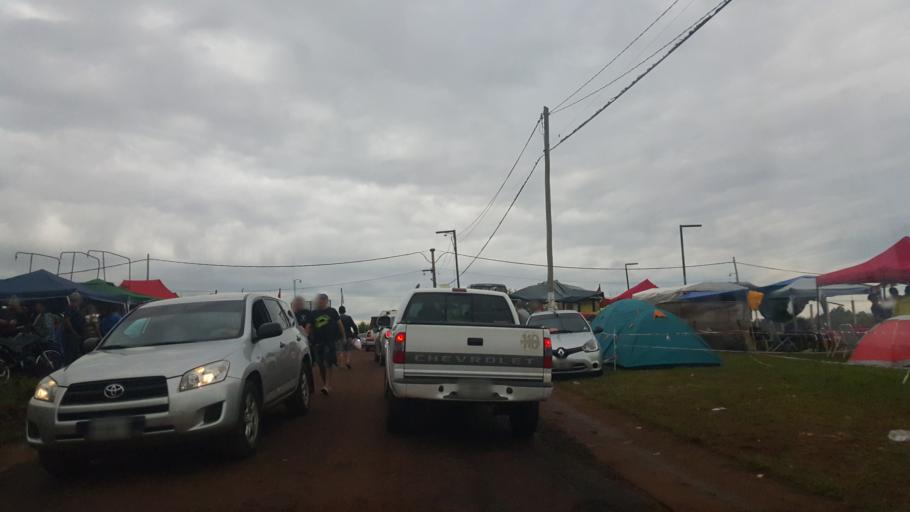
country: AR
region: Misiones
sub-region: Departamento de Capital
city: Posadas
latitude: -27.4356
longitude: -55.9254
